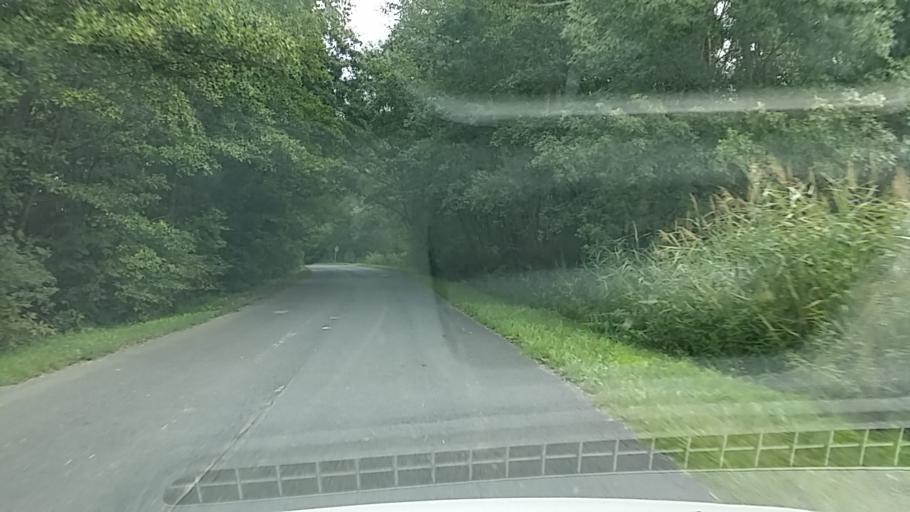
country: HU
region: Gyor-Moson-Sopron
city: Lebeny
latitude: 47.7273
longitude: 17.3222
